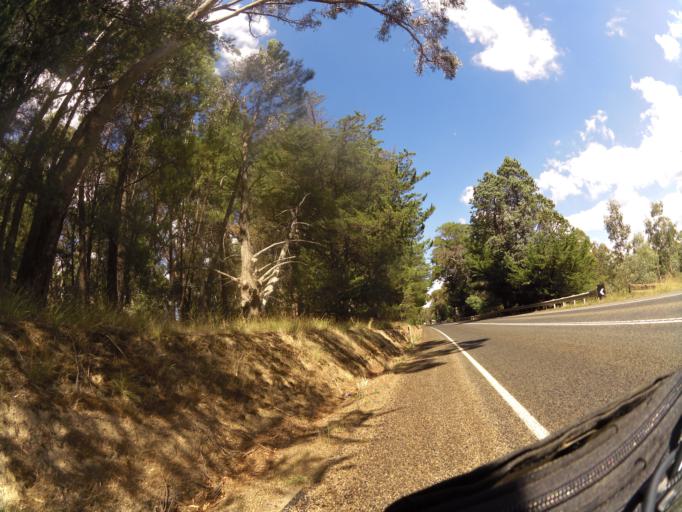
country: AU
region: Victoria
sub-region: Mansfield
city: Mansfield
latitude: -36.8270
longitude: 146.0082
